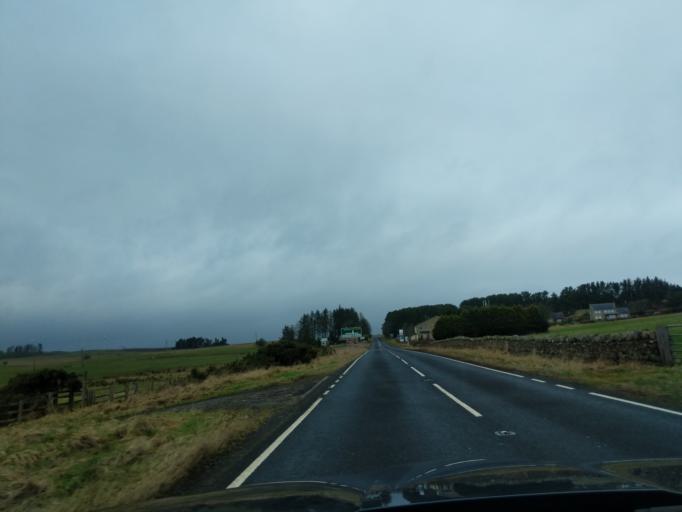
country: GB
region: England
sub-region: Northumberland
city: Rothley
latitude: 55.1635
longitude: -2.0178
